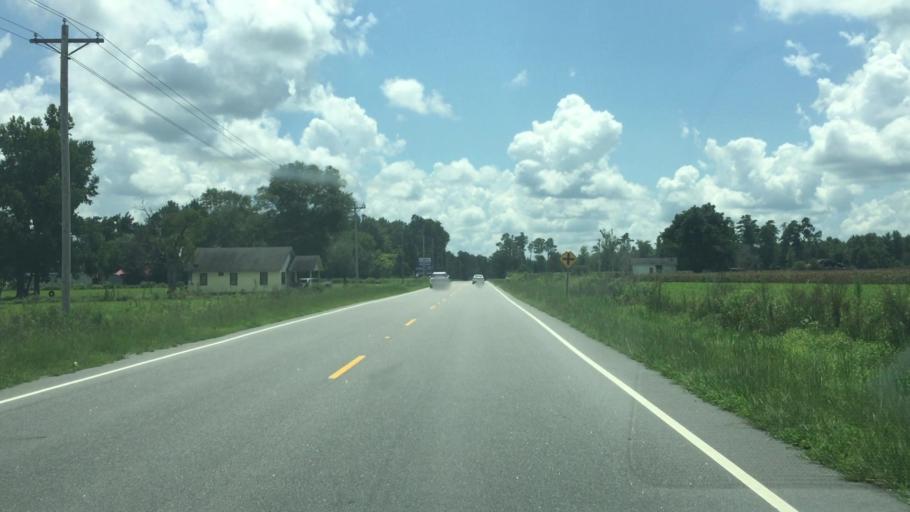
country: US
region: North Carolina
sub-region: Columbus County
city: Tabor City
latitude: 34.2217
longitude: -78.8241
